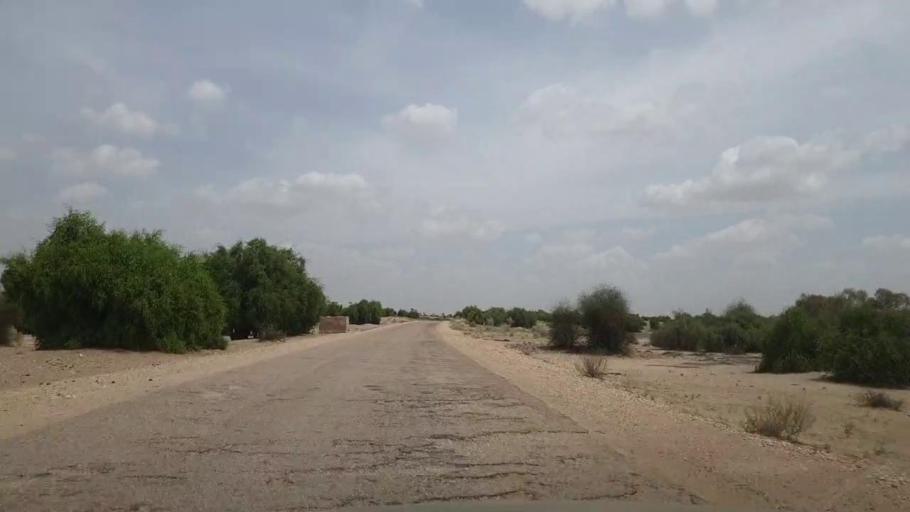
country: PK
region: Sindh
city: Kot Diji
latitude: 27.1929
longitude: 69.1654
